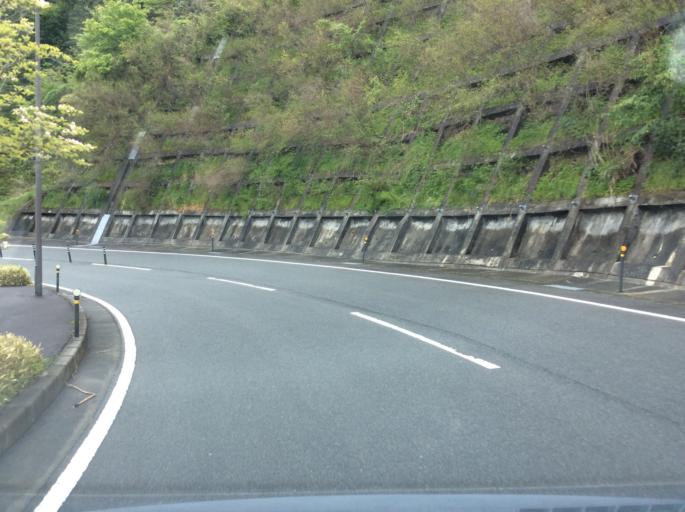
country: JP
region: Fukushima
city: Iwaki
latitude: 37.0382
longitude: 140.9278
